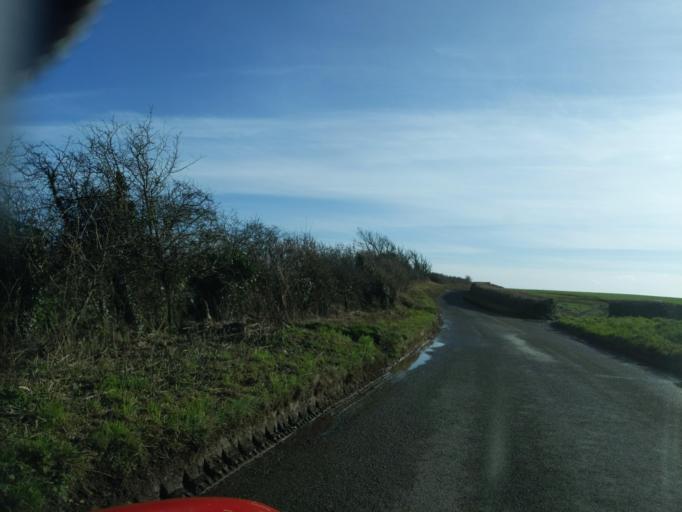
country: GB
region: England
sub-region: Devon
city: Kingsbridge
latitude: 50.3436
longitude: -3.7255
